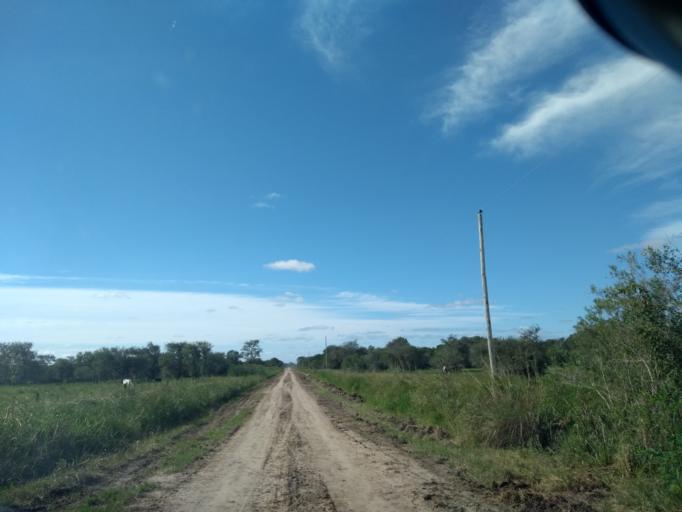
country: AR
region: Chaco
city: Colonia Benitez
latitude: -27.2880
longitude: -58.9324
